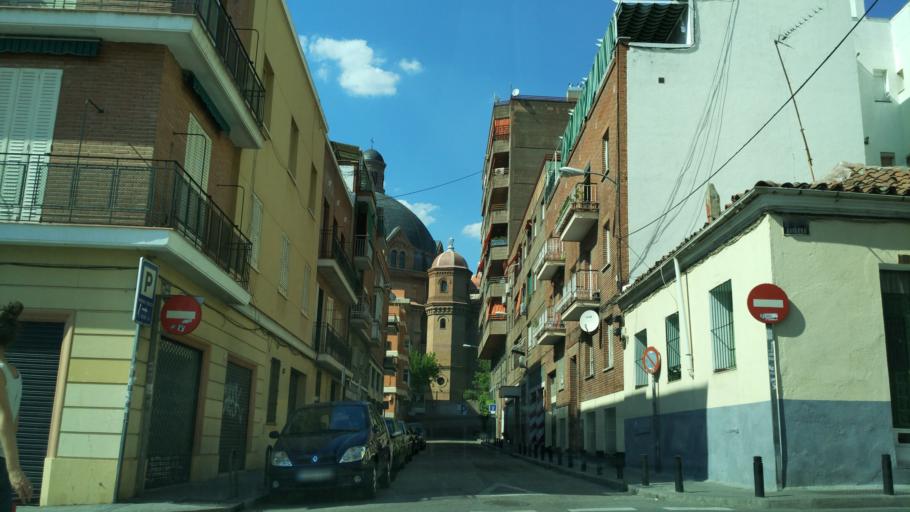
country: ES
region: Madrid
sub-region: Provincia de Madrid
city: Tetuan de las Victorias
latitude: 40.4535
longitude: -3.7038
